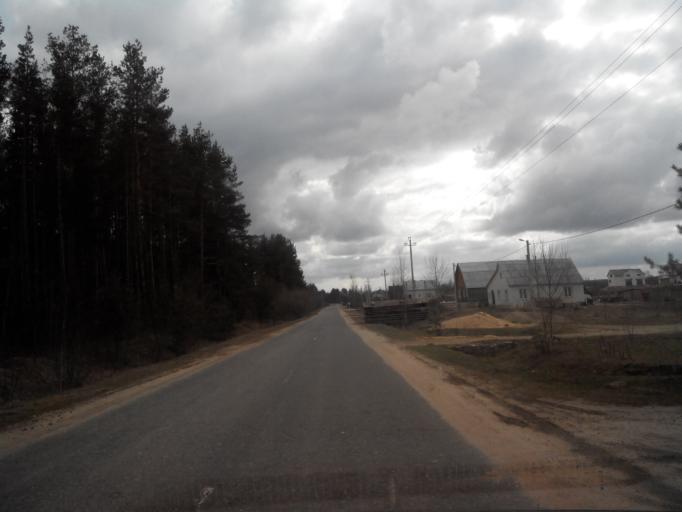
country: BY
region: Vitebsk
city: Pastavy
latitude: 55.0913
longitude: 26.8400
